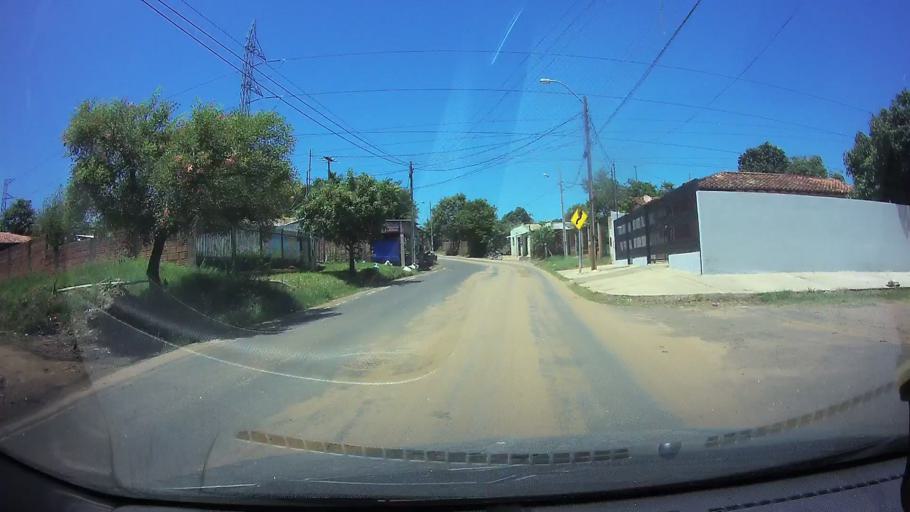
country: PY
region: Central
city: San Lorenzo
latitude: -25.3291
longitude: -57.4861
